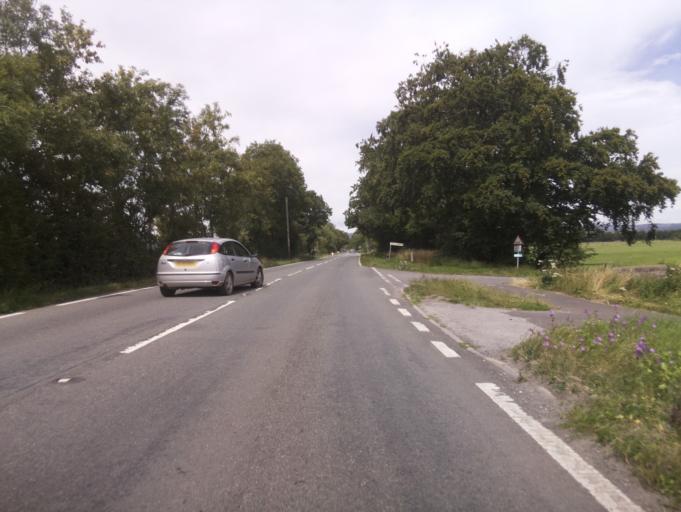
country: GB
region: England
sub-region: Somerset
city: Glastonbury
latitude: 51.1687
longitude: -2.6975
